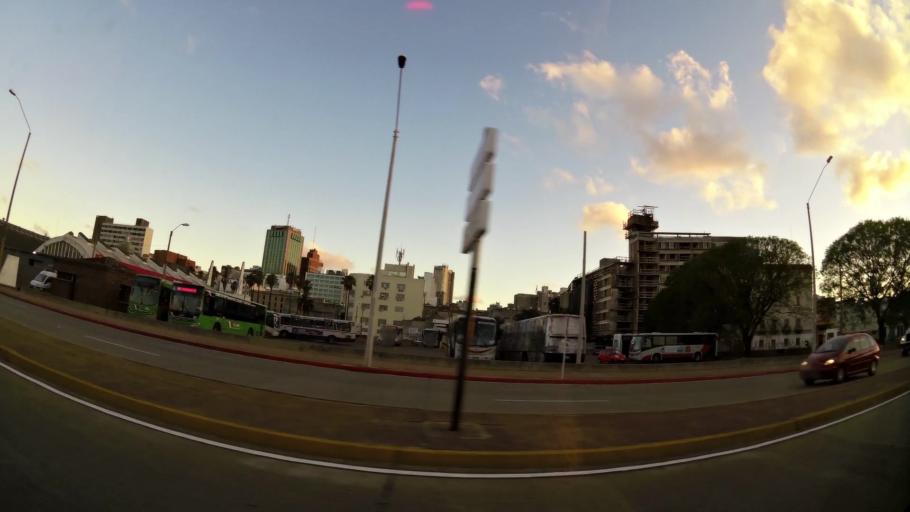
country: UY
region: Montevideo
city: Montevideo
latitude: -34.9021
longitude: -56.2032
